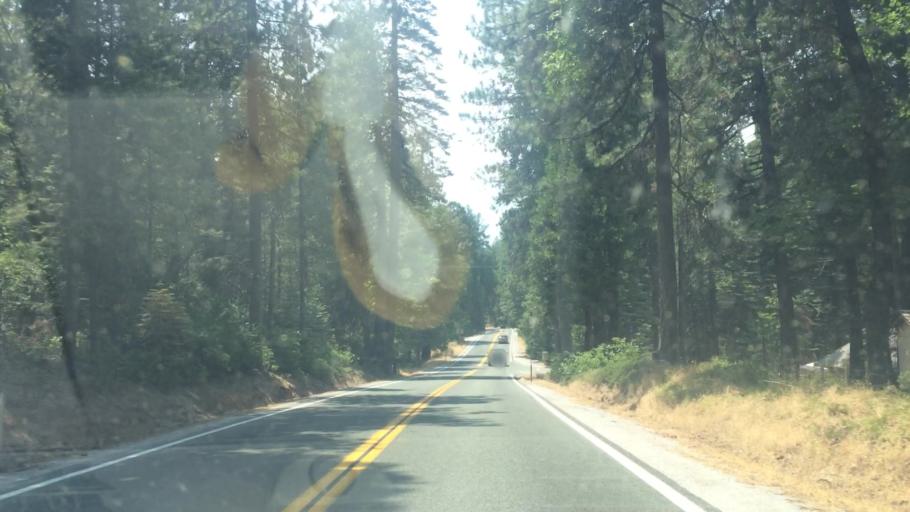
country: US
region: California
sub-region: Amador County
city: Pioneer
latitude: 38.5037
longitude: -120.4969
